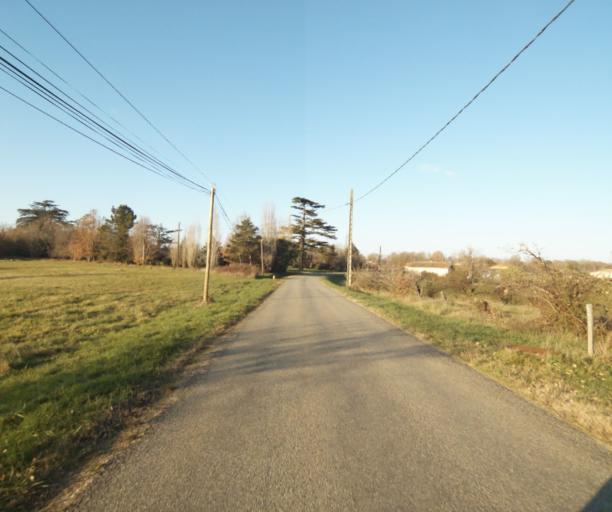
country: FR
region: Midi-Pyrenees
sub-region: Departement du Tarn-et-Garonne
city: Moissac
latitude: 44.1464
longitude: 1.1223
